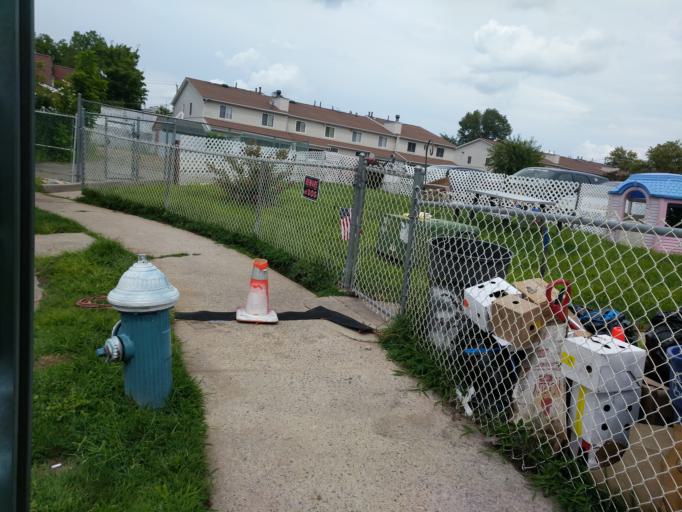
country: US
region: New York
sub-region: Richmond County
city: Bloomfield
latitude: 40.6179
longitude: -74.1568
